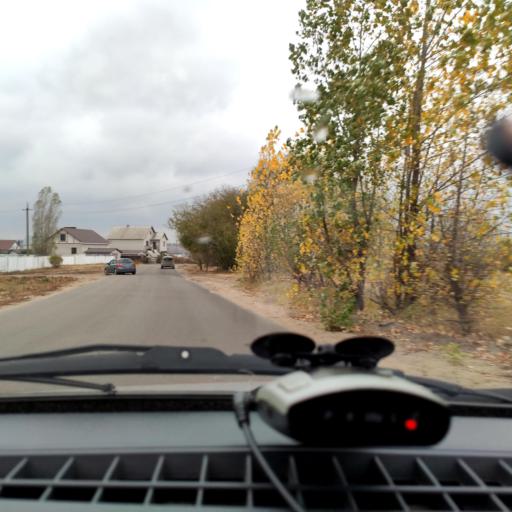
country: RU
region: Voronezj
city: Pridonskoy
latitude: 51.6994
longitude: 39.0748
